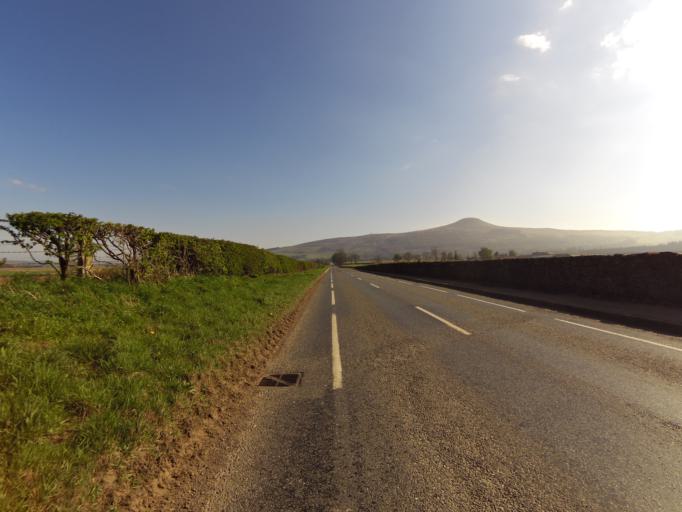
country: GB
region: Scotland
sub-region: Fife
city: Falkland
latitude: 56.2695
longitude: -3.2105
